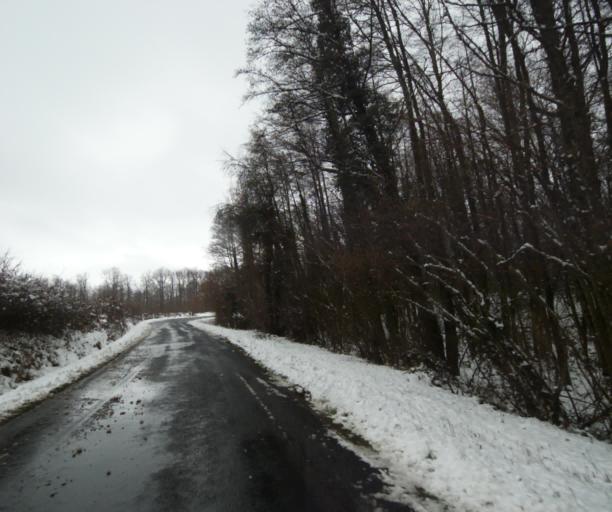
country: FR
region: Champagne-Ardenne
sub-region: Departement de la Haute-Marne
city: Laneuville-a-Remy
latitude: 48.4630
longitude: 4.8551
